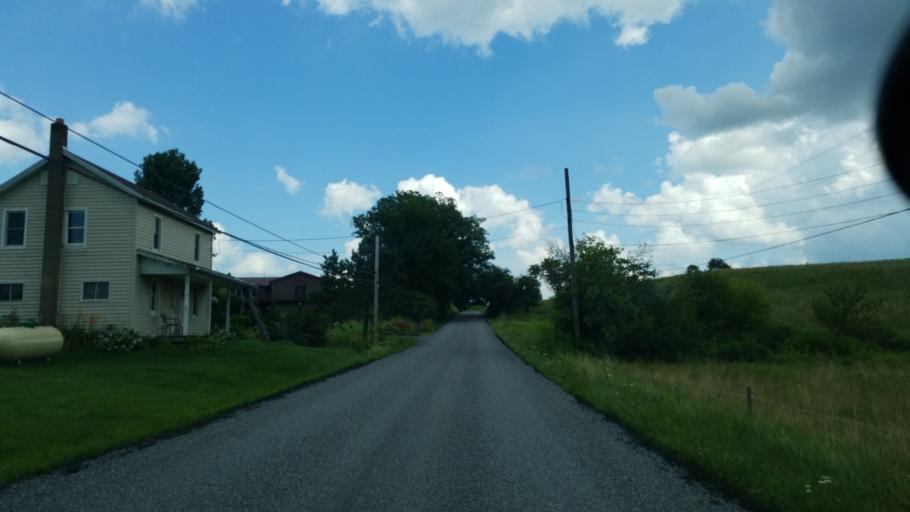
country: US
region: Pennsylvania
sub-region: Jefferson County
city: Brookville
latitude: 41.2315
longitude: -79.0054
